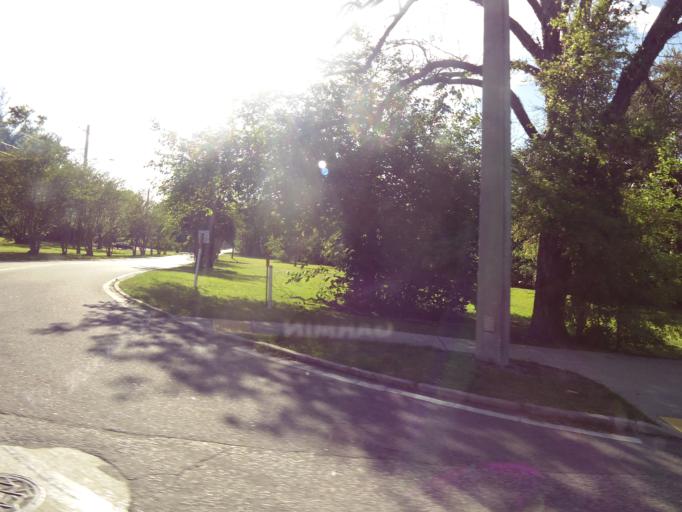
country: US
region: Florida
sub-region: Duval County
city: Jacksonville
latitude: 30.3276
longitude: -81.6909
